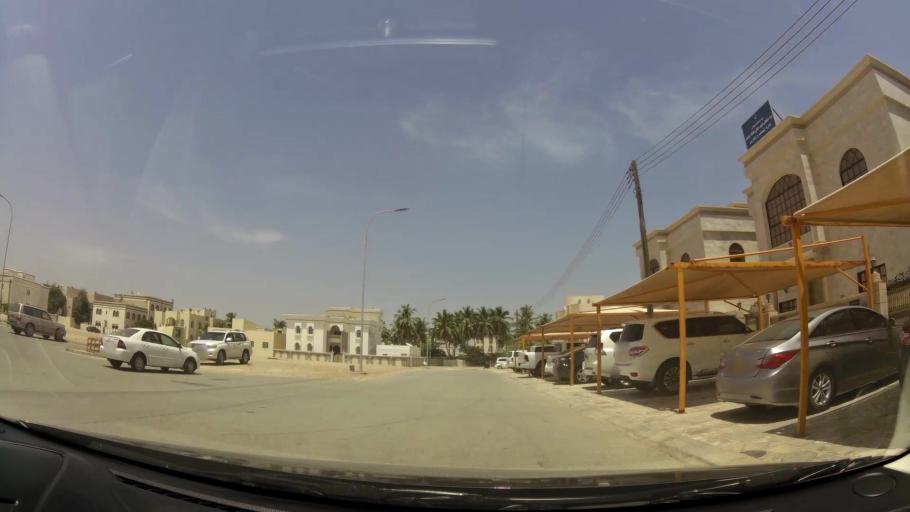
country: OM
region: Zufar
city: Salalah
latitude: 17.0664
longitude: 54.1516
